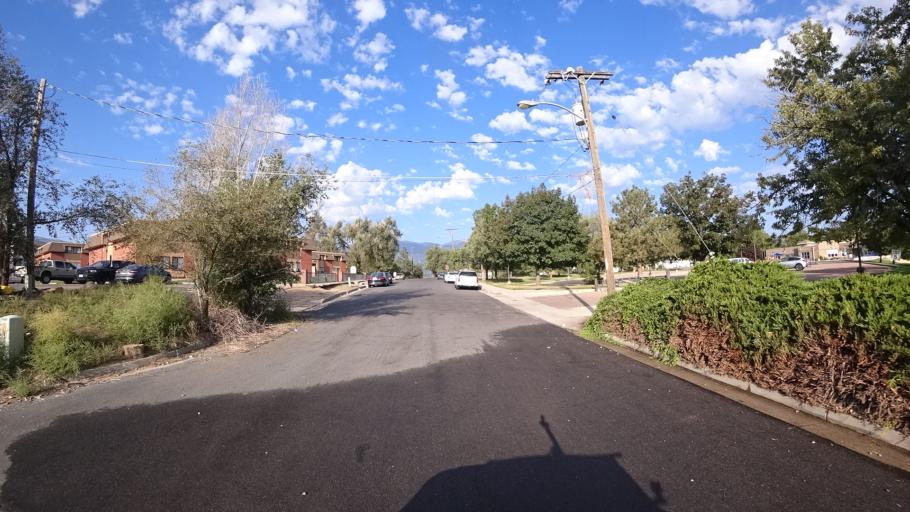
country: US
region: Colorado
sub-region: El Paso County
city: Colorado Springs
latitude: 38.8195
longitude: -104.8070
